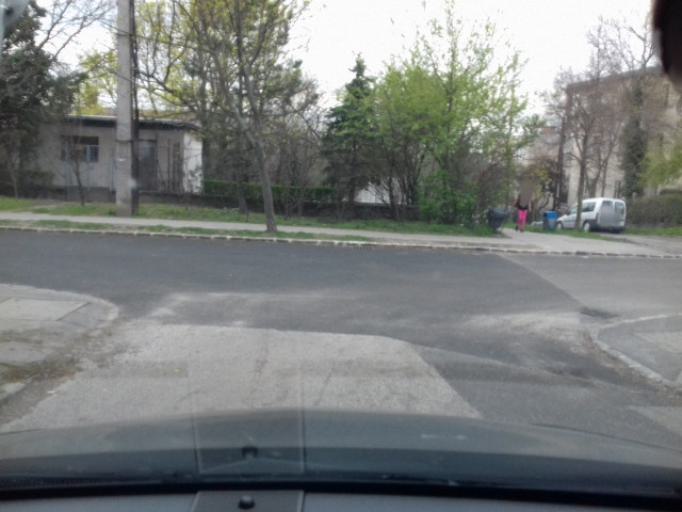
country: HU
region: Budapest
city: Budapest XI. keruelet
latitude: 47.4838
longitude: 19.0341
